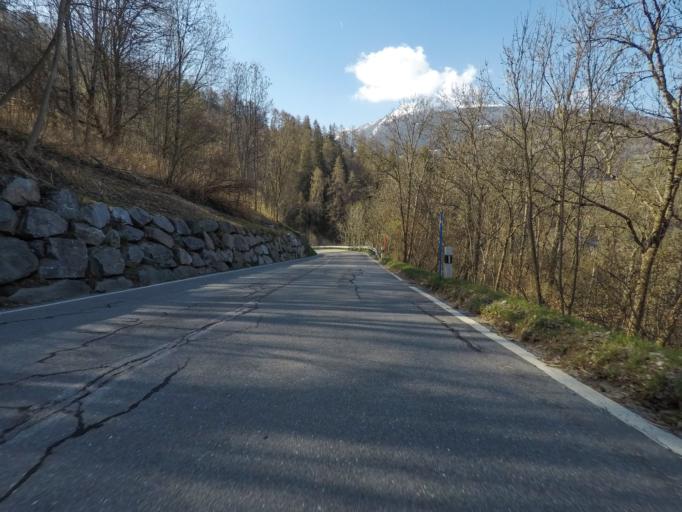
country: CH
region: Valais
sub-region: Conthey District
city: Basse-Nendaz
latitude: 46.1871
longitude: 7.3302
